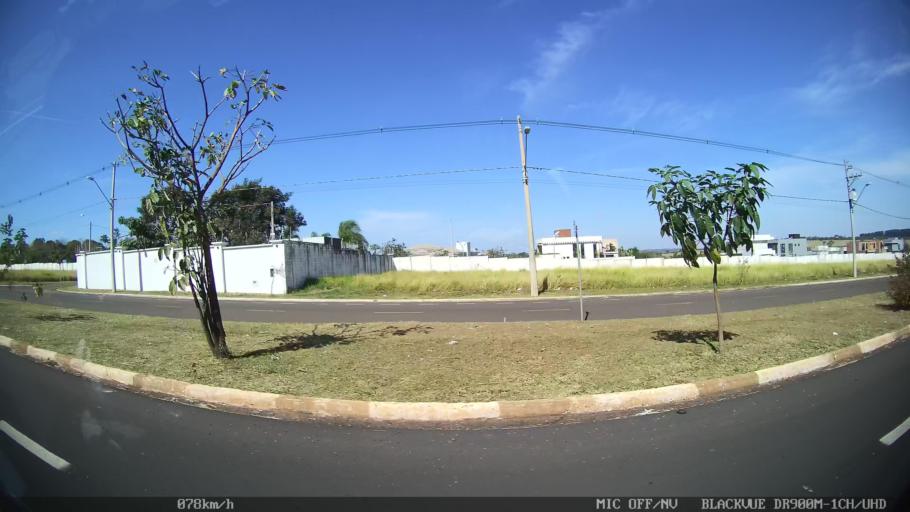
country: BR
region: Sao Paulo
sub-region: Franca
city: Franca
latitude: -20.5525
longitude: -47.4338
